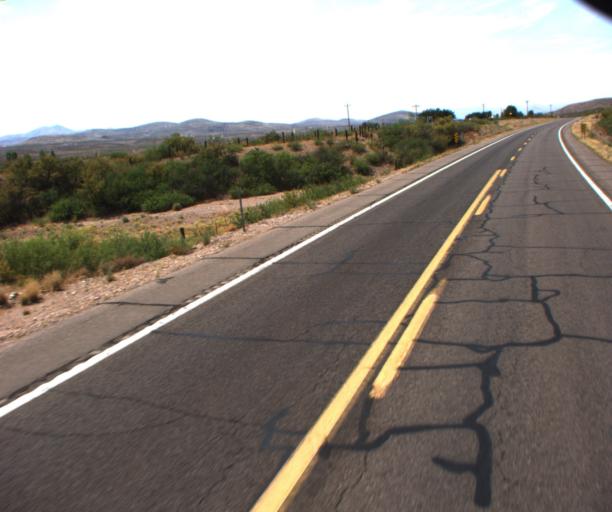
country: US
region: Arizona
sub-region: Greenlee County
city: Clifton
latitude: 32.8174
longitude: -109.1718
